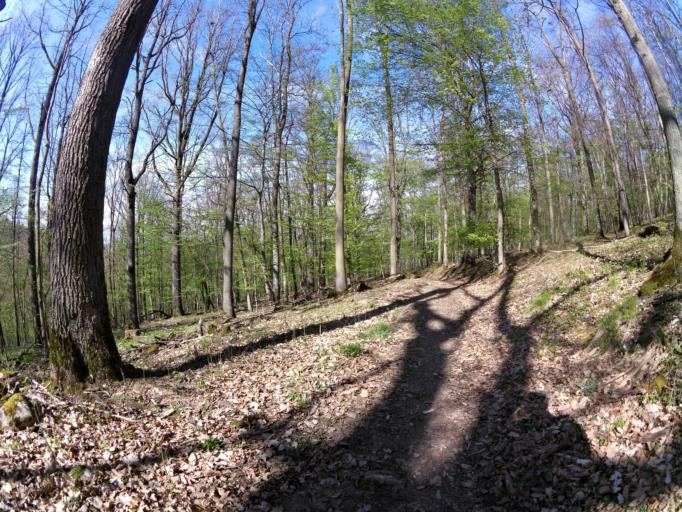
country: DE
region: Bavaria
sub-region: Regierungsbezirk Unterfranken
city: Winterhausen
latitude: 49.6995
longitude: 10.0055
